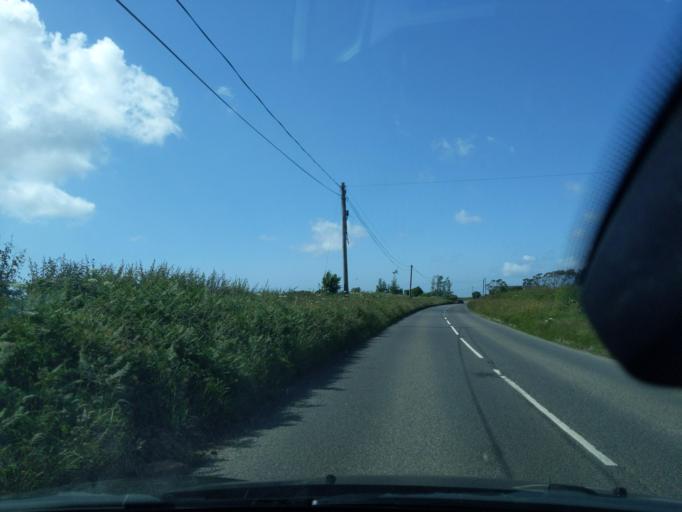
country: GB
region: England
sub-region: Devon
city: Great Torrington
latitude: 51.0010
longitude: -4.1012
